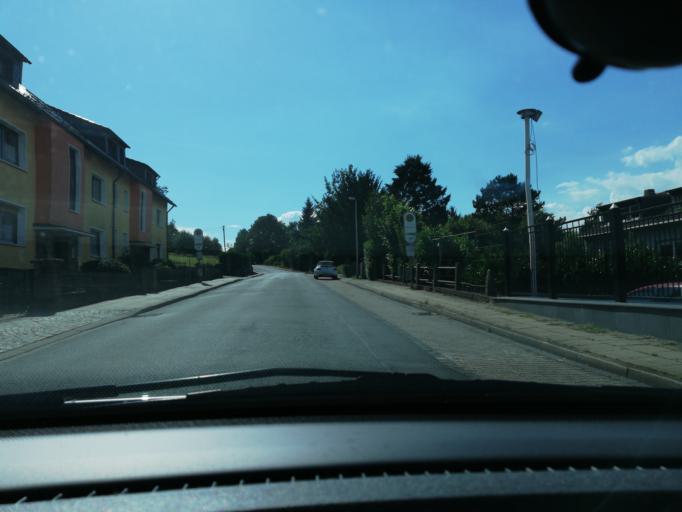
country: DE
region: North Rhine-Westphalia
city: Witten
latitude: 51.4475
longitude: 7.3890
